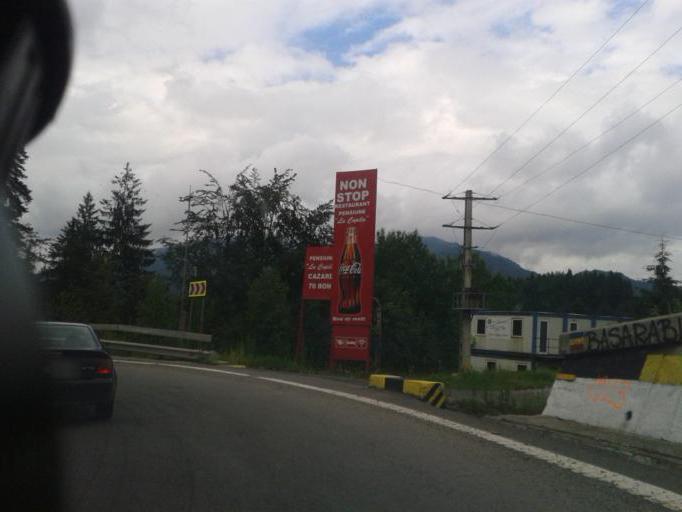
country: RO
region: Brasov
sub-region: Oras Predeal
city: Predeal
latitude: 45.5175
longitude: 25.5796
